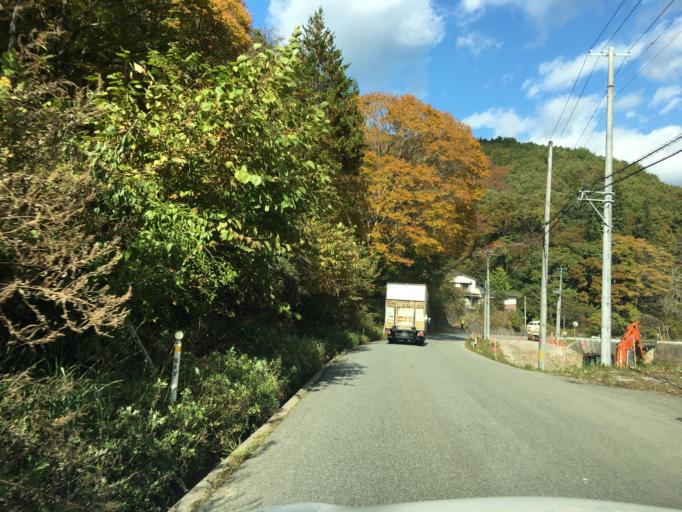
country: JP
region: Fukushima
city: Namie
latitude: 37.3503
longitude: 140.8923
